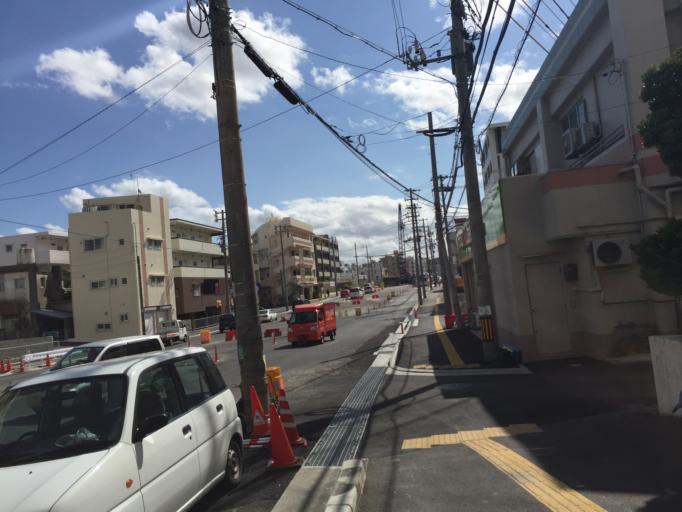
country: JP
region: Okinawa
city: Ginowan
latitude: 26.2337
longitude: 127.7286
